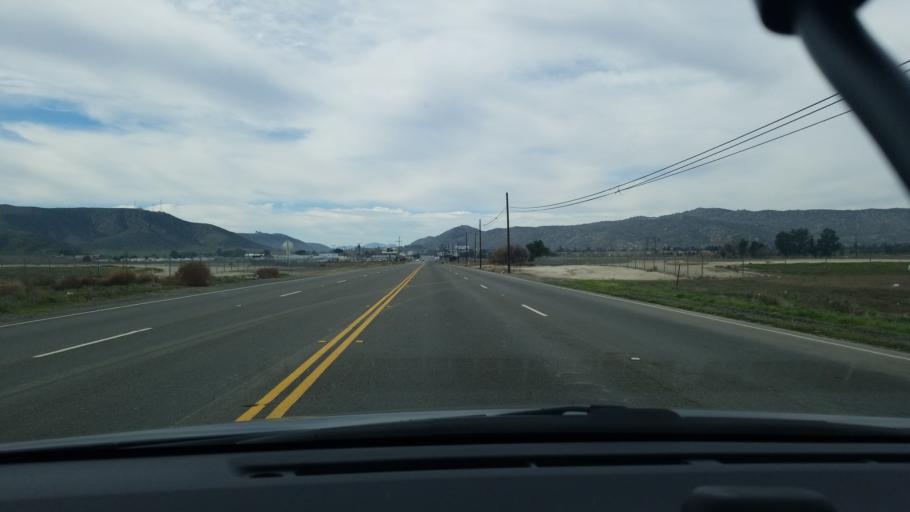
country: US
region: California
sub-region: Riverside County
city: Green Acres
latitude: 33.7439
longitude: -117.0380
